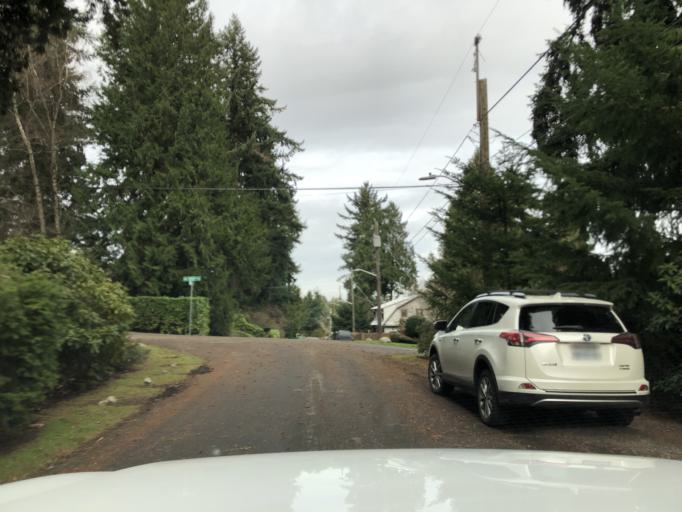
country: US
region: Washington
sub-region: King County
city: Inglewood-Finn Hill
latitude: 47.7009
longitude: -122.2752
